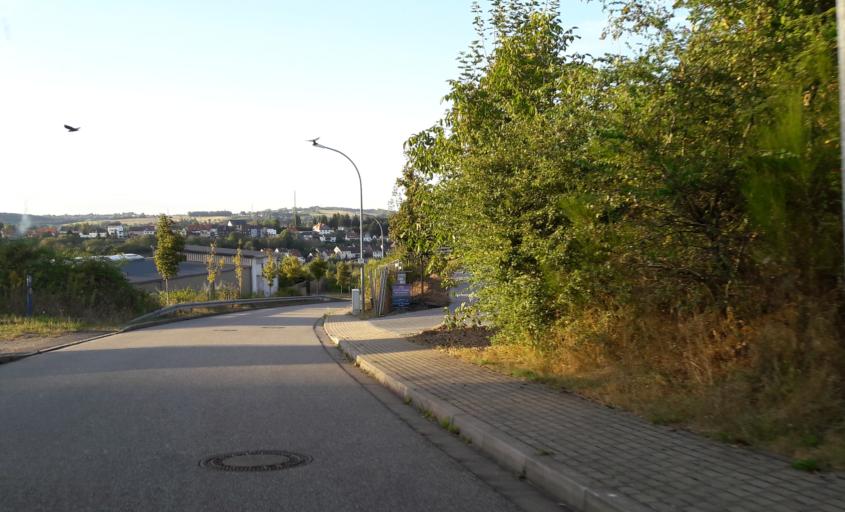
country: DE
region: Saarland
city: Schiffweiler
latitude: 49.3481
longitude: 7.1274
